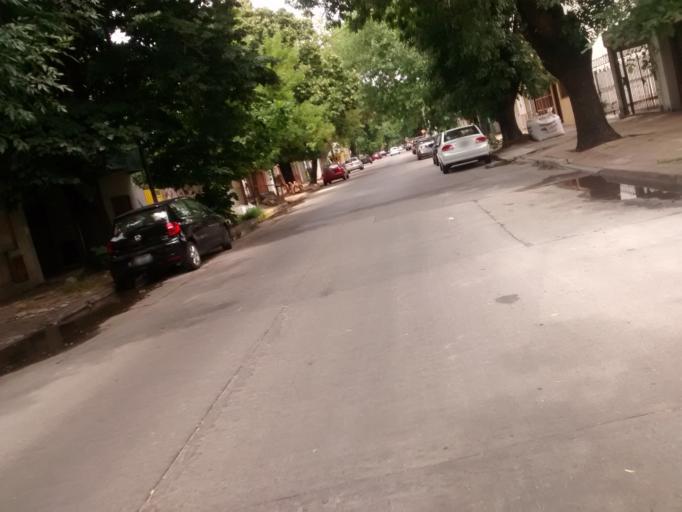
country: AR
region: Buenos Aires
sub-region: Partido de La Plata
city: La Plata
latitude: -34.9323
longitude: -57.9335
